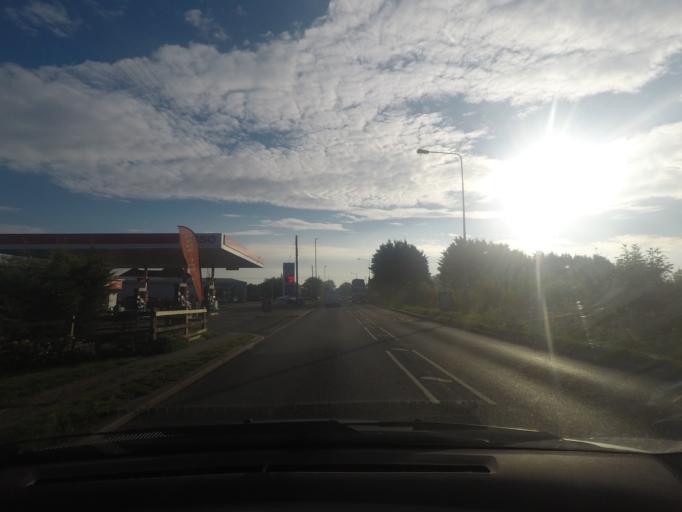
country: GB
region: England
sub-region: City of York
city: Holtby
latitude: 53.9550
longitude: -0.9735
